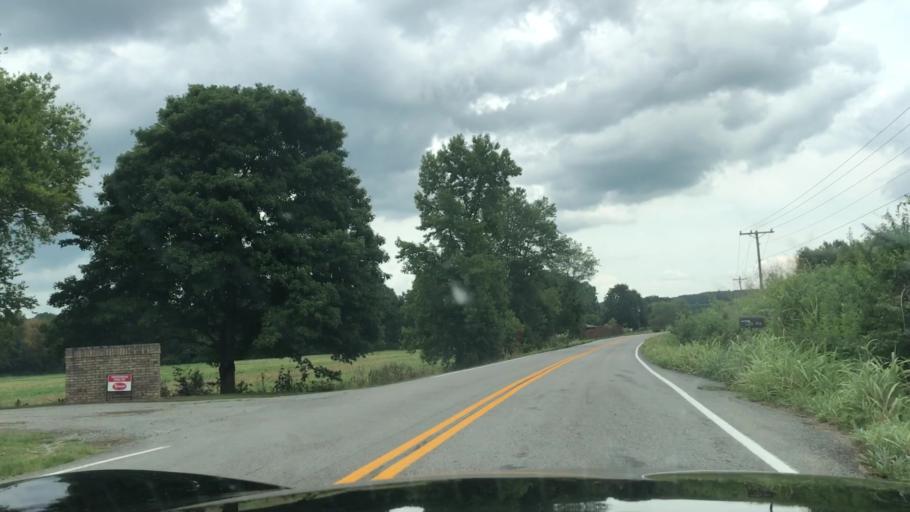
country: US
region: Kentucky
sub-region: Muhlenberg County
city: Central City
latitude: 37.2046
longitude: -87.0175
